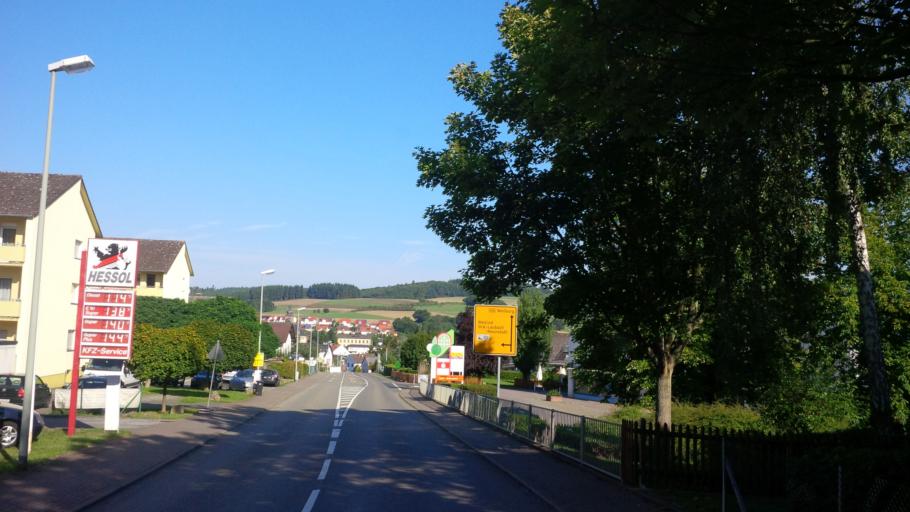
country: DE
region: Hesse
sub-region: Regierungsbezirk Darmstadt
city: Gravenwiesbach
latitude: 50.3828
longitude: 8.4613
